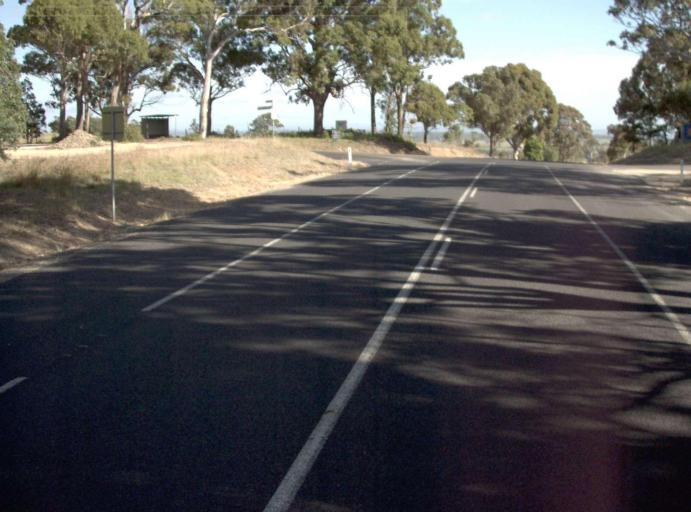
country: AU
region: Victoria
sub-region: East Gippsland
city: Lakes Entrance
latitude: -37.8583
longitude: 147.8454
